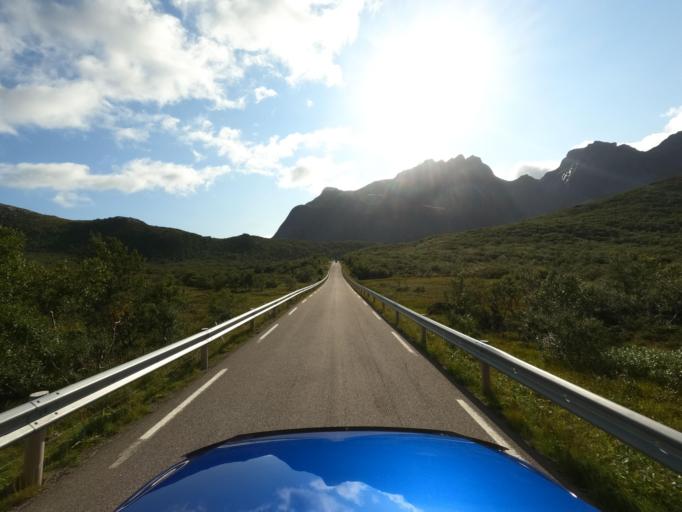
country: NO
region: Nordland
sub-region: Flakstad
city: Ramberg
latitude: 68.0680
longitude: 13.3317
